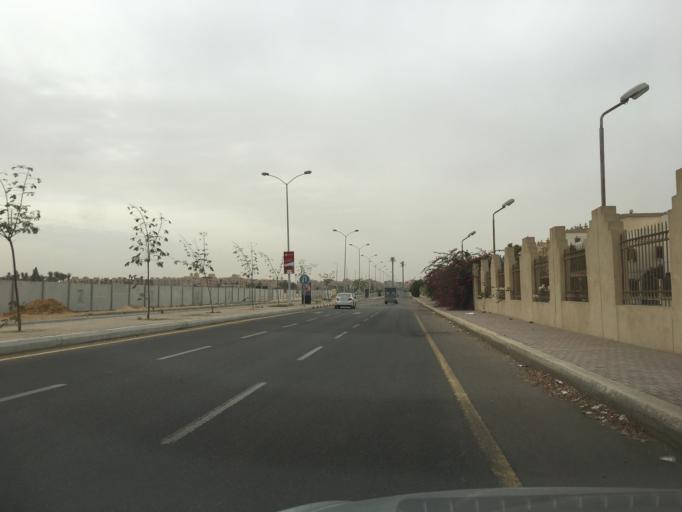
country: EG
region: Al Jizah
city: Awsim
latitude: 30.0476
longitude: 30.9972
